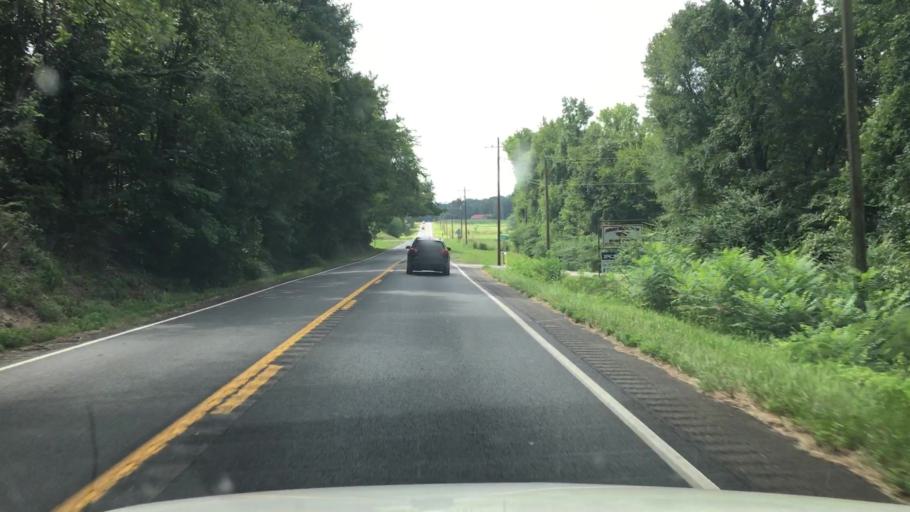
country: US
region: Arkansas
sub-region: Garland County
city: Lake Hamilton
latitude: 34.3376
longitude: -93.1803
